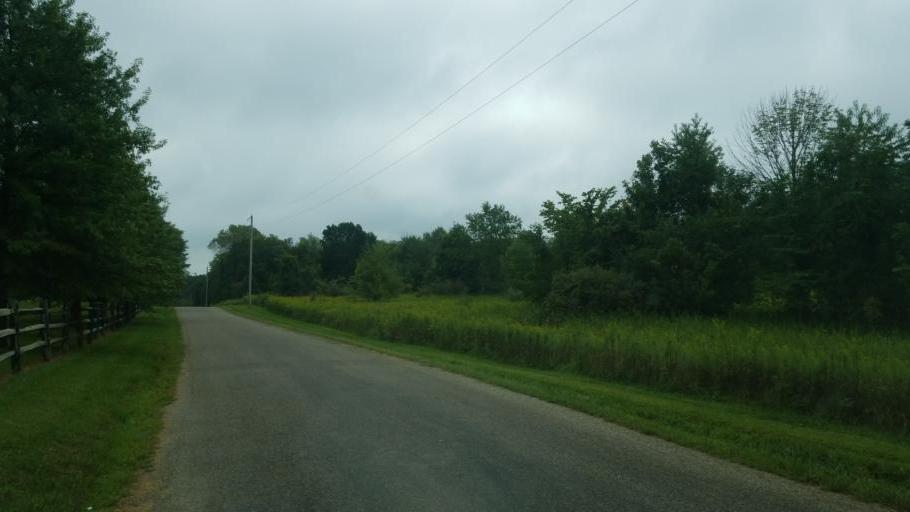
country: US
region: Ohio
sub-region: Licking County
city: Utica
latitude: 40.2546
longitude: -82.4361
